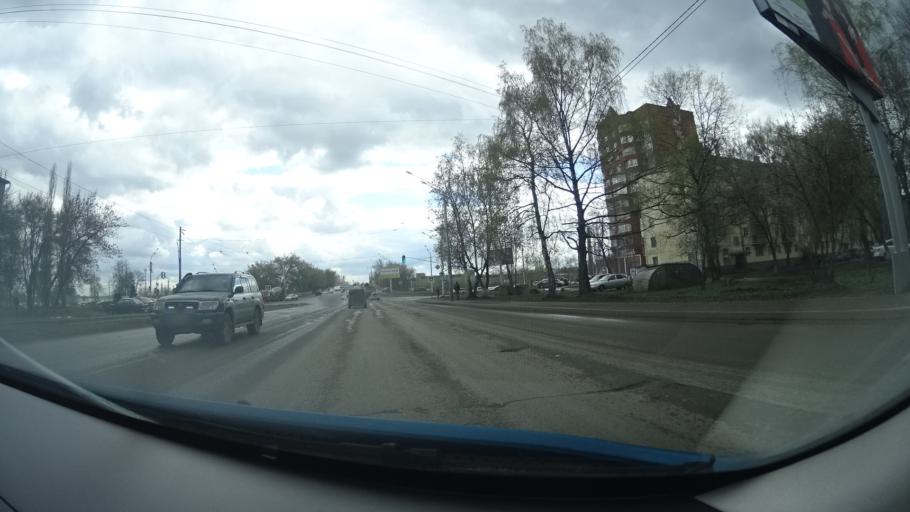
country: RU
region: Bashkortostan
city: Ufa
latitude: 54.8115
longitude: 56.0880
